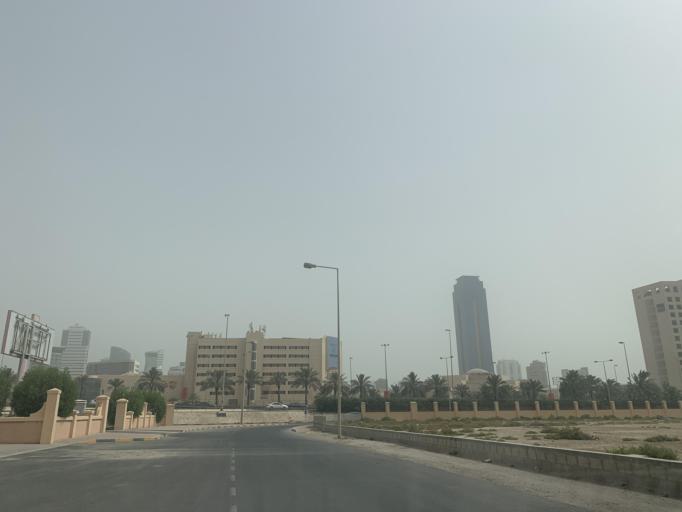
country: BH
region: Manama
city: Jidd Hafs
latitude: 26.2301
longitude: 50.5388
